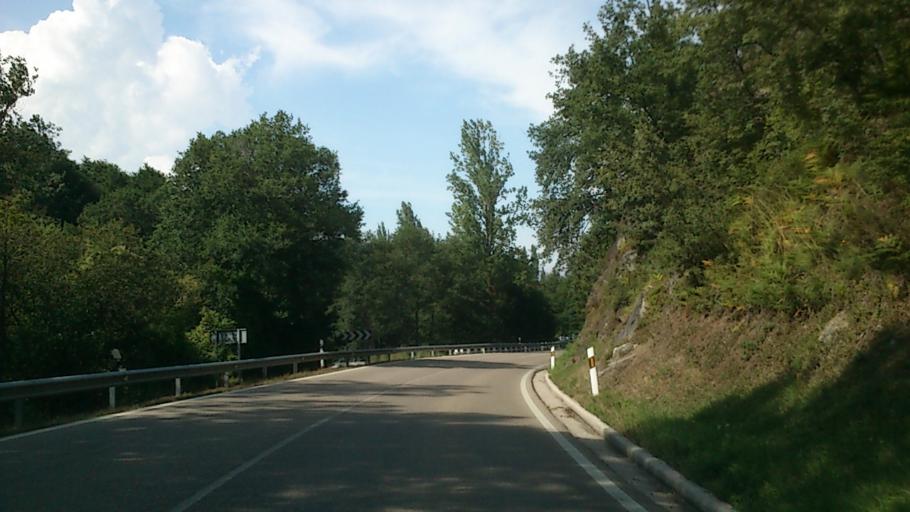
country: ES
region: Castille and Leon
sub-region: Provincia de Burgos
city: Medina de Pomar
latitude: 43.0200
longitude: -3.4834
